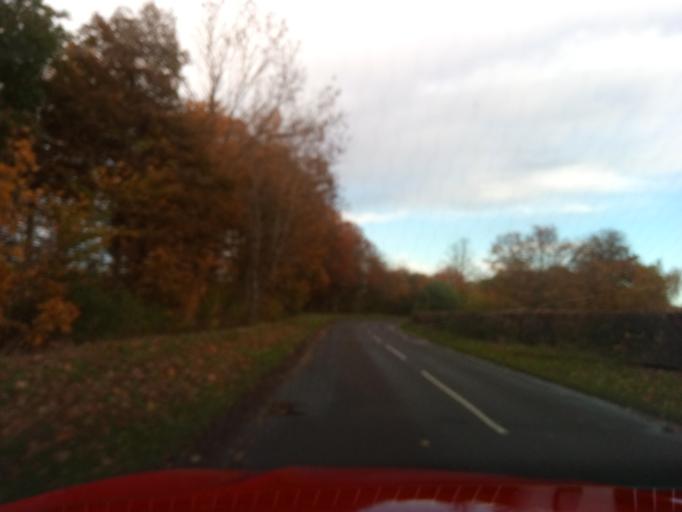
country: GB
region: England
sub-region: Northumberland
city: Ford
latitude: 55.6284
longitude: -2.1064
